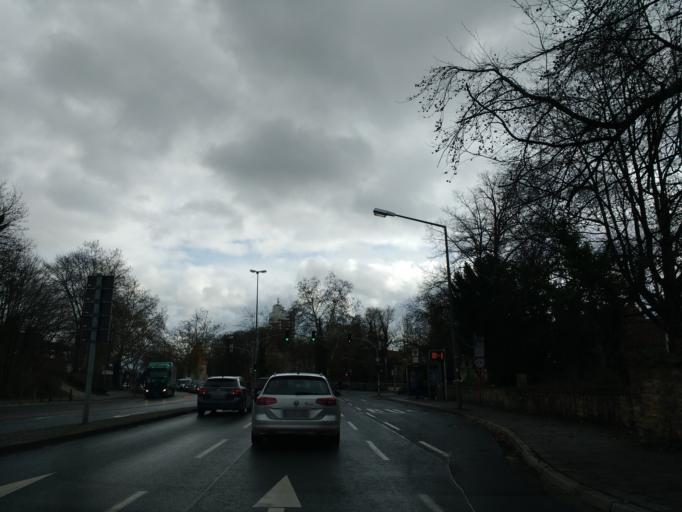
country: DE
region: Lower Saxony
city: Osnabrueck
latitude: 52.2819
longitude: 8.0434
